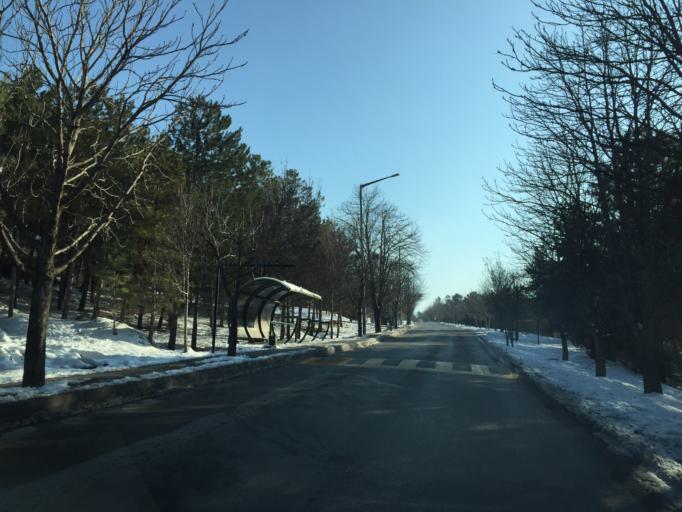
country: TR
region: Ankara
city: Ankara
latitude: 39.8927
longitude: 32.7811
